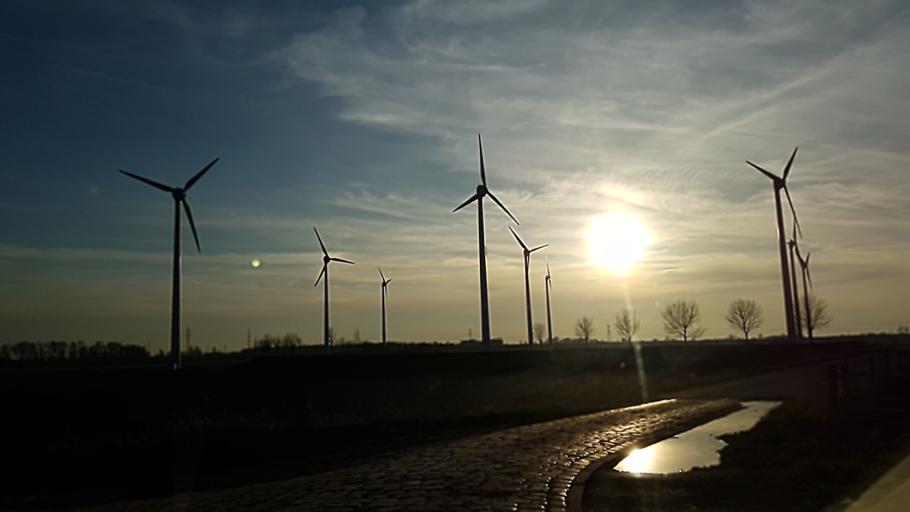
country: NL
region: North Brabant
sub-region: Gemeente Woensdrecht
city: Woensdrecht
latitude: 51.3834
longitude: 4.2740
